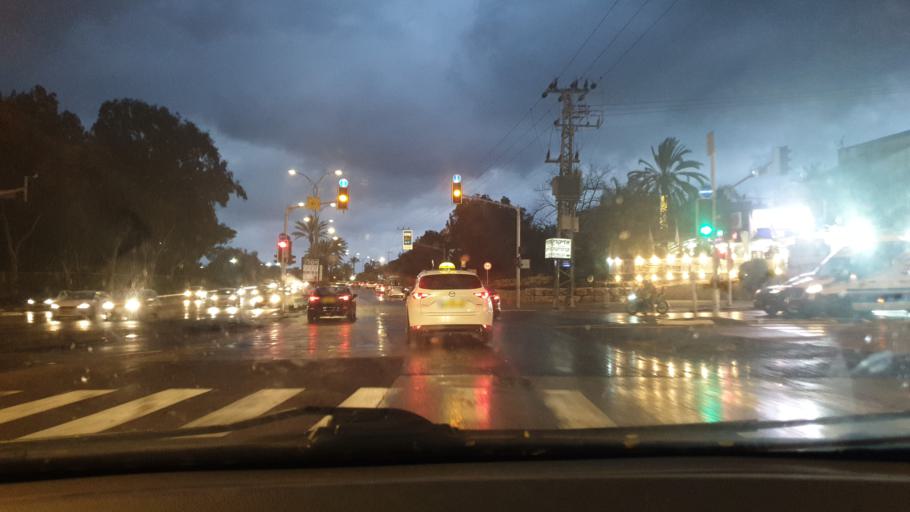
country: IL
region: Central District
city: Rishon LeZiyyon
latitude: 31.9778
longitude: 34.7910
